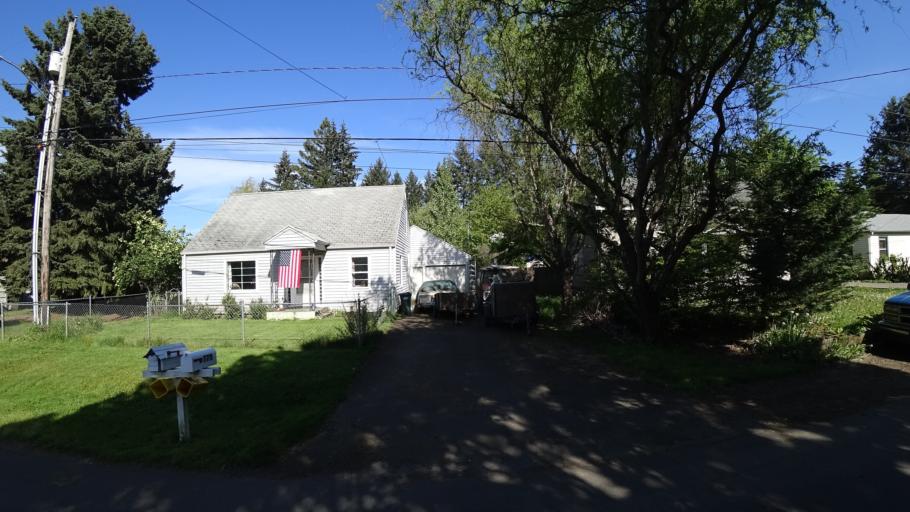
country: US
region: Oregon
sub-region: Washington County
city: Hillsboro
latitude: 45.5298
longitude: -122.9845
